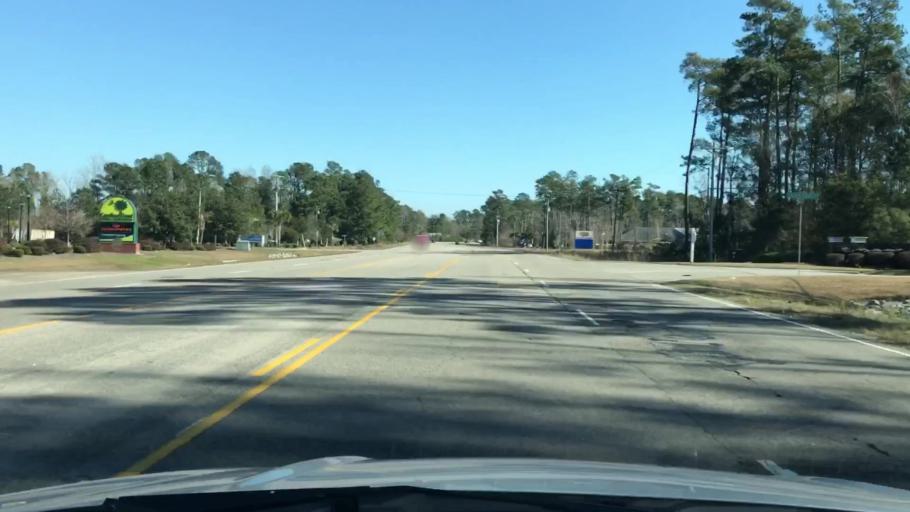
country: US
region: South Carolina
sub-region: Horry County
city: Garden City
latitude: 33.6300
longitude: -79.0250
